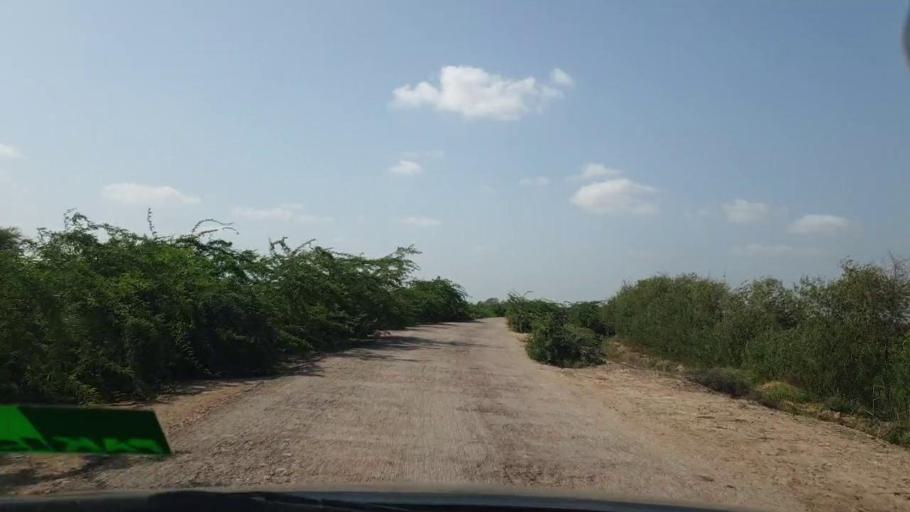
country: PK
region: Sindh
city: Tando Bago
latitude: 24.6657
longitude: 69.1978
